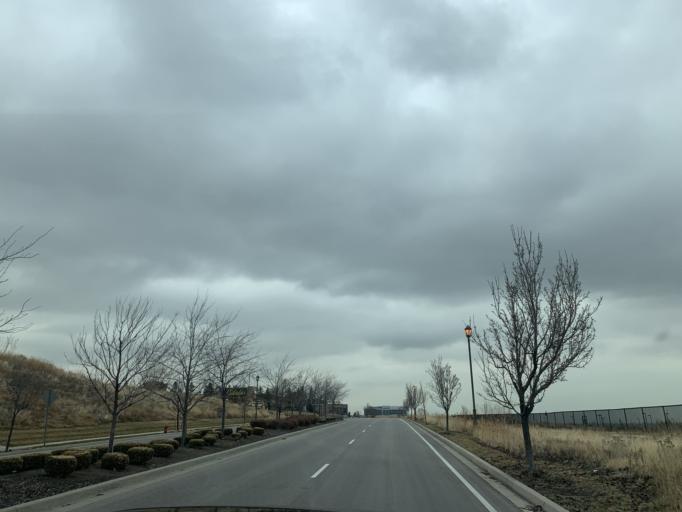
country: US
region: Utah
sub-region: Utah County
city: Lehi
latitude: 40.4360
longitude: -111.8899
